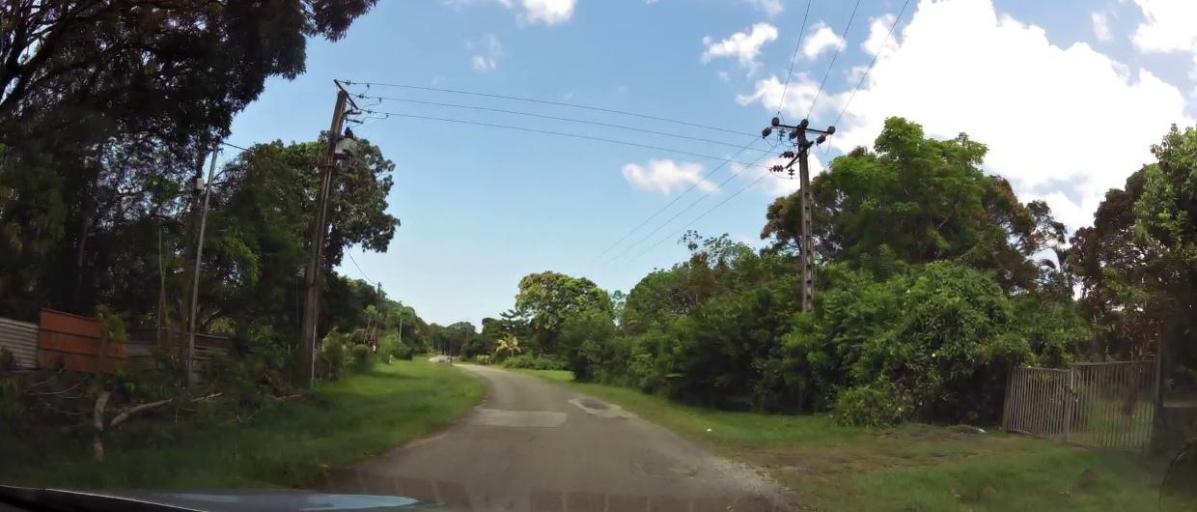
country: GF
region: Guyane
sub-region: Guyane
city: Matoury
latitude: 4.8319
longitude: -52.3082
